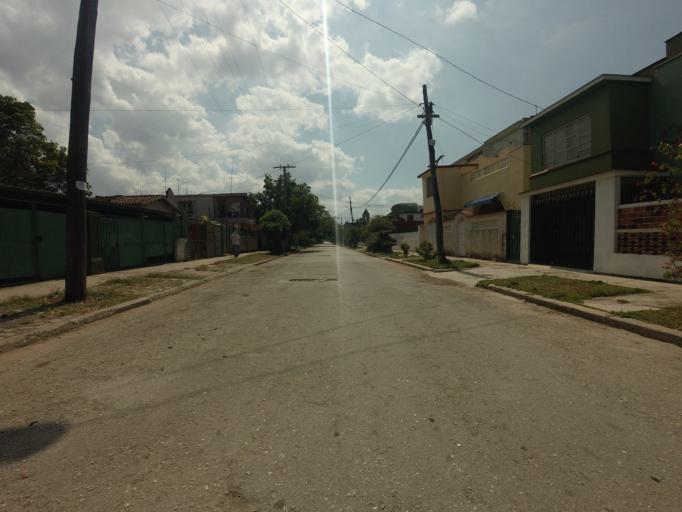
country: CU
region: La Habana
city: Cerro
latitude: 23.1063
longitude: -82.4271
